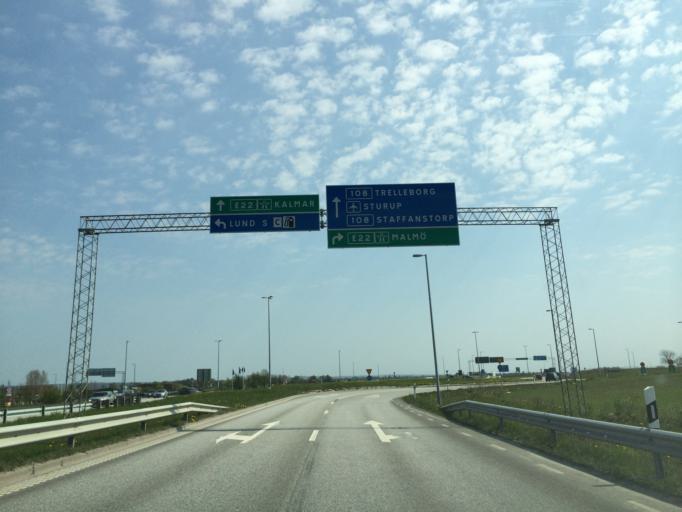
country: SE
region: Skane
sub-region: Lunds Kommun
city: Lund
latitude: 55.6799
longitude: 13.1784
